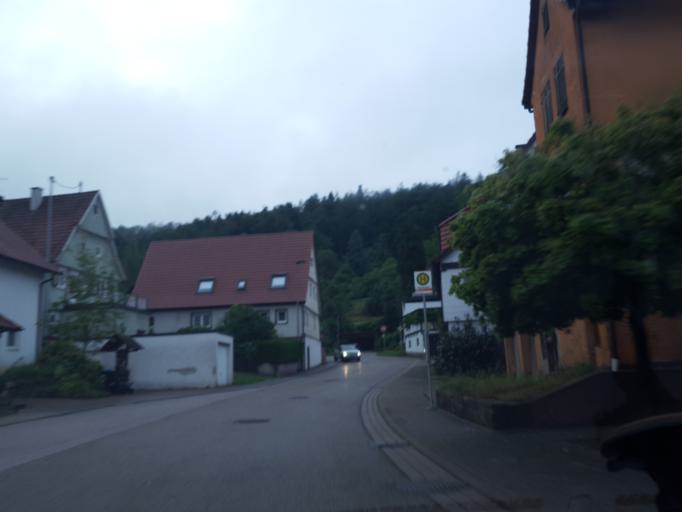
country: DE
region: Baden-Wuerttemberg
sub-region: Regierungsbezirk Stuttgart
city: Rudersberg
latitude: 48.8595
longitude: 9.5106
